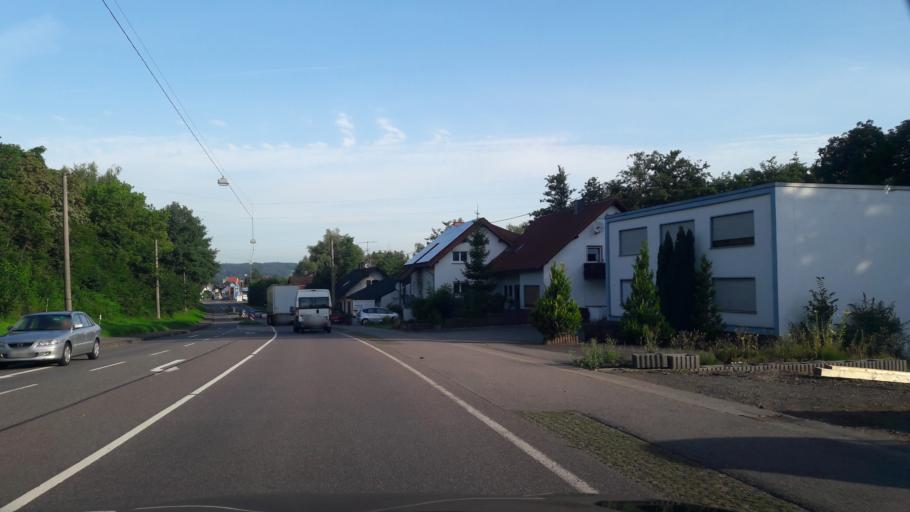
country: DE
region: Saarland
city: Lebach
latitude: 49.4004
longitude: 6.9198
